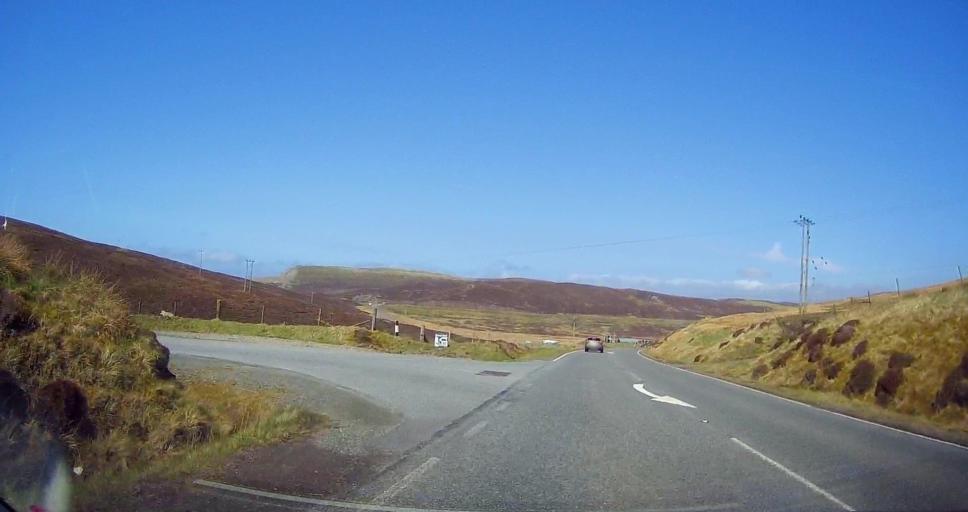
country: GB
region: Scotland
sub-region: Shetland Islands
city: Lerwick
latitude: 60.1379
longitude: -1.2330
